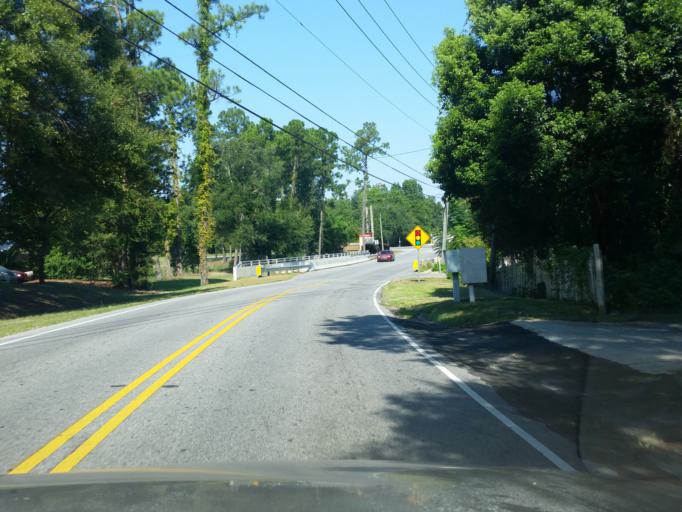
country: US
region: Florida
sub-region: Escambia County
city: Ferry Pass
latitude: 30.5174
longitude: -87.2190
